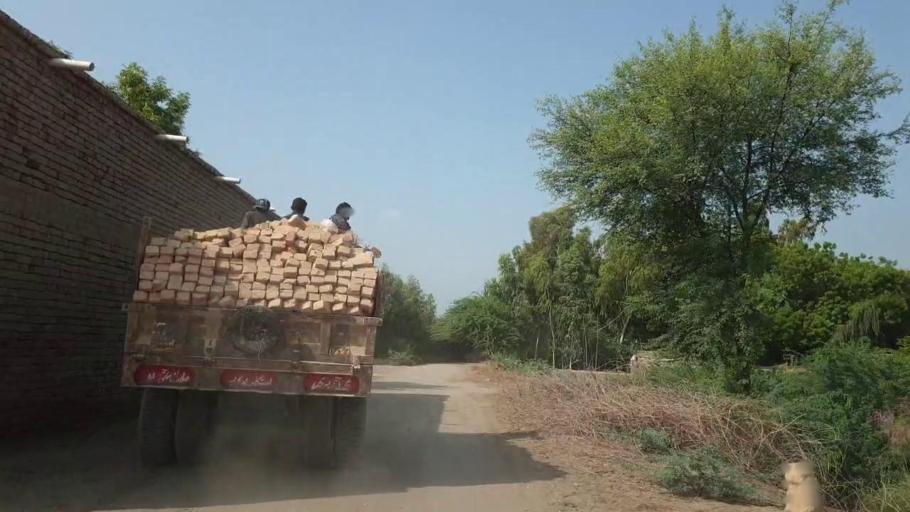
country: PK
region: Sindh
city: Larkana
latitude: 27.4814
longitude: 68.2532
